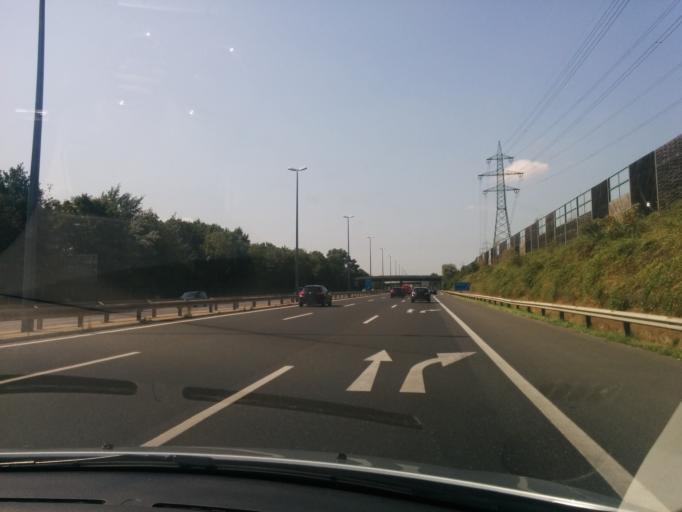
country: AT
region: Lower Austria
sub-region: Politischer Bezirk Korneuburg
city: Langenzersdorf
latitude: 48.2764
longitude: 16.3695
